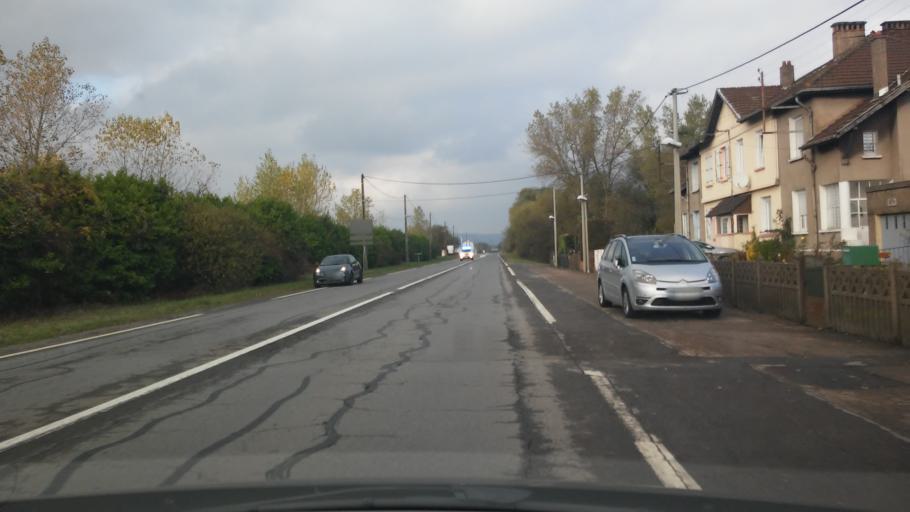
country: FR
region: Lorraine
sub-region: Departement de la Moselle
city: Uckange
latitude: 49.3159
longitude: 6.1570
